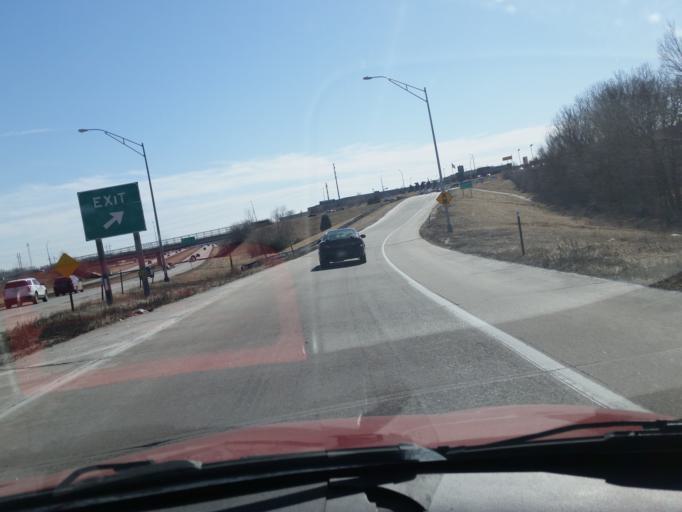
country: US
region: Nebraska
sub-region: Sarpy County
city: Offutt Air Force Base
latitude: 41.1618
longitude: -95.9393
